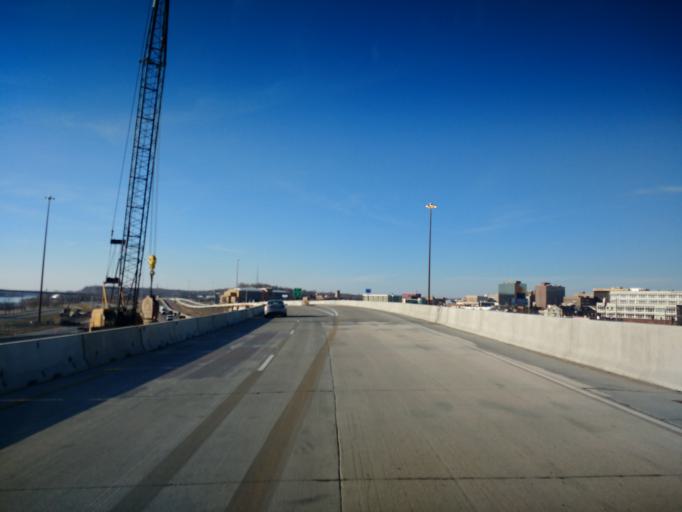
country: US
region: Iowa
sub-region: Woodbury County
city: Sioux City
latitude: 42.4876
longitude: -96.3961
